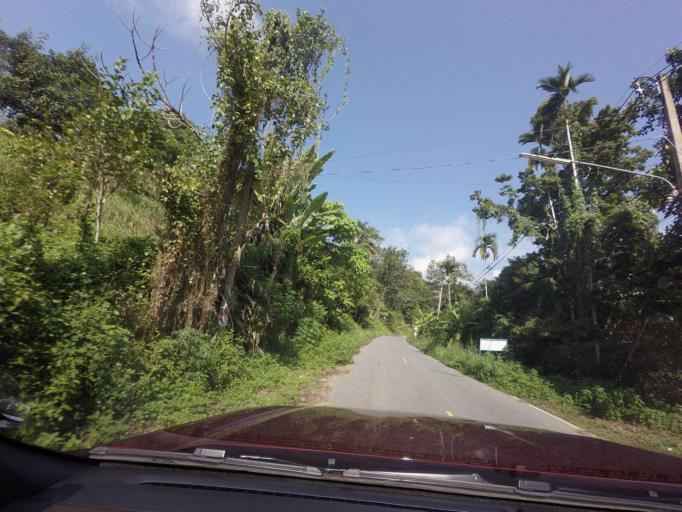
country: TH
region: Yala
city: Than To
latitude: 5.9978
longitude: 101.2176
